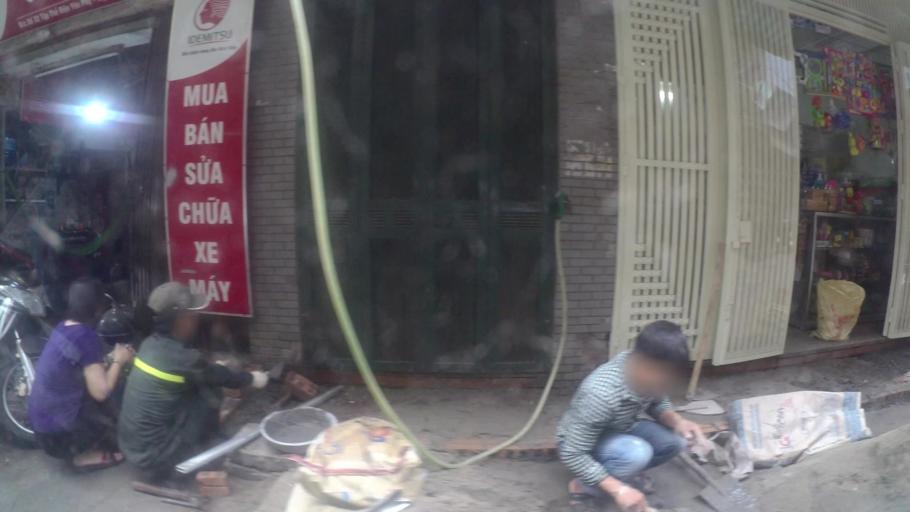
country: VN
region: Ha Noi
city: Hoan Kiem
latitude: 21.0511
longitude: 105.8425
